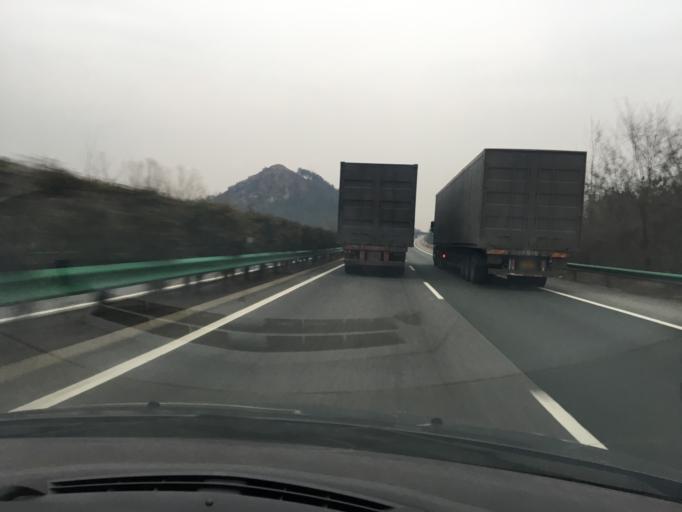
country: CN
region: Hubei
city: Taipingqiao
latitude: 31.0663
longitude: 114.6381
